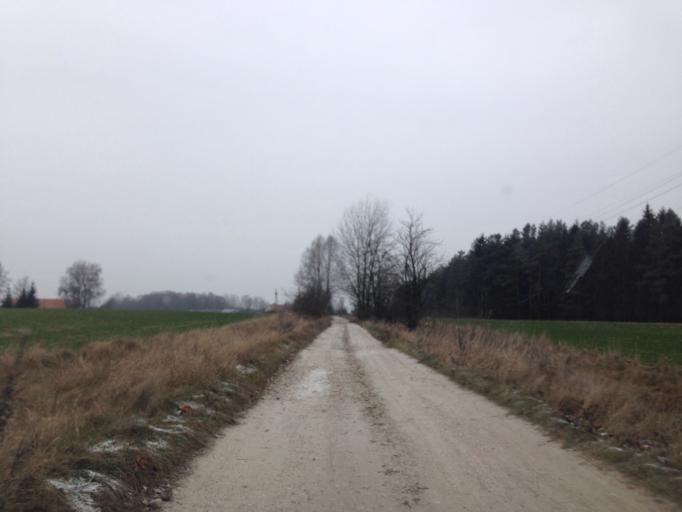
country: PL
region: Warmian-Masurian Voivodeship
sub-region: Powiat ketrzynski
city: Reszel
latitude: 54.0500
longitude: 21.2055
